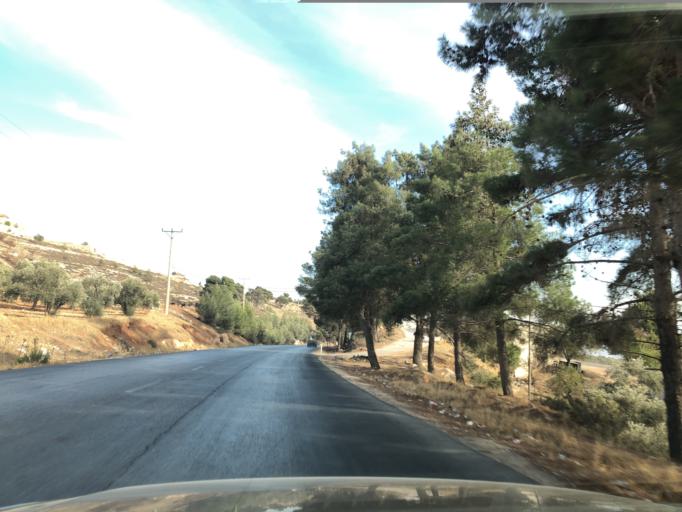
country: JO
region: Irbid
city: Al Kittah
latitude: 32.2876
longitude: 35.8548
